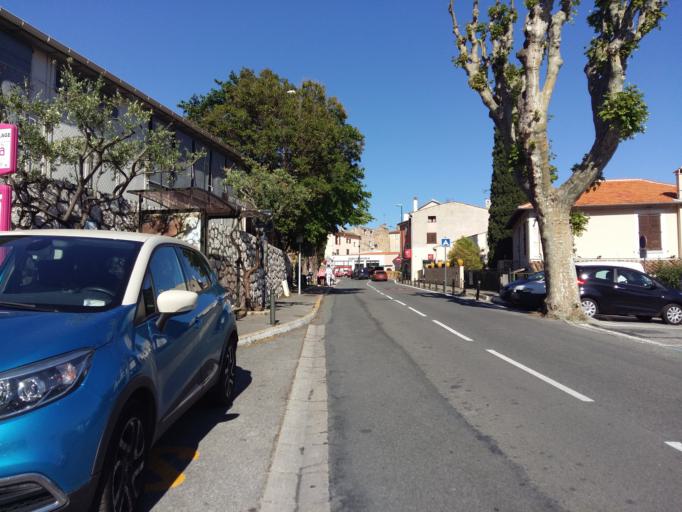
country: FR
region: Provence-Alpes-Cote d'Azur
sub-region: Departement des Alpes-Maritimes
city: Biot
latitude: 43.6278
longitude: 7.0954
